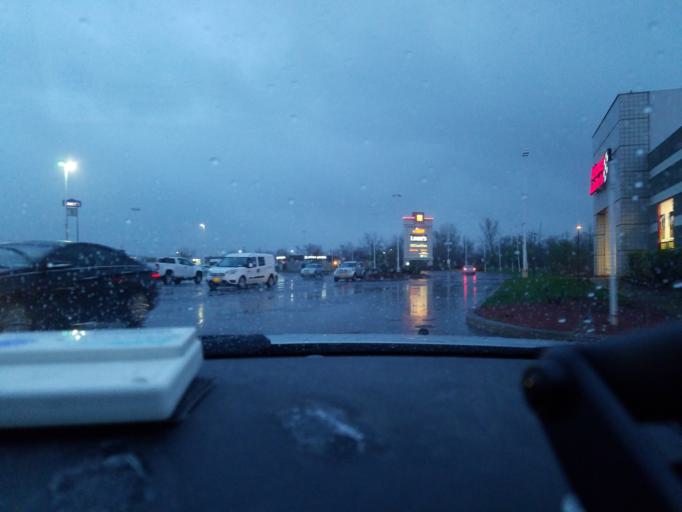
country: US
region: New York
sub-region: Onondaga County
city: North Syracuse
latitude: 43.1496
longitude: -76.1218
